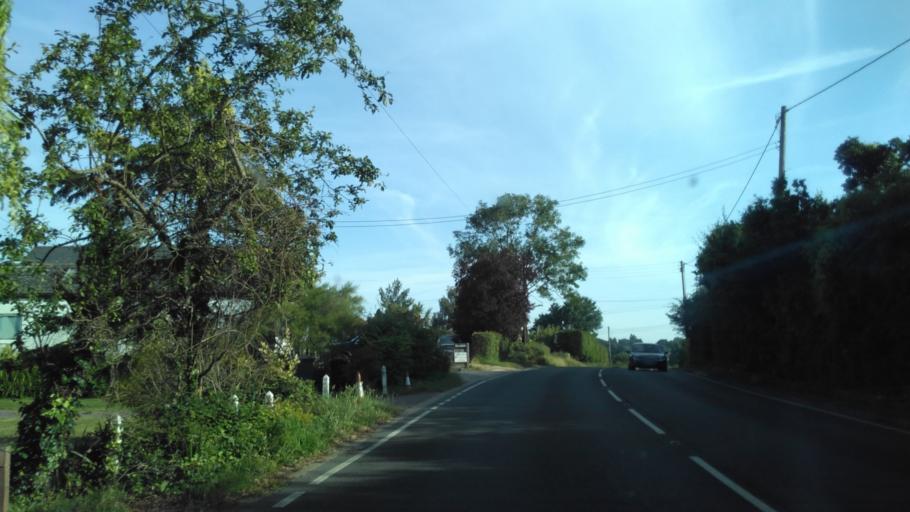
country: GB
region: England
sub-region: Kent
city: Blean
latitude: 51.3291
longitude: 1.0246
